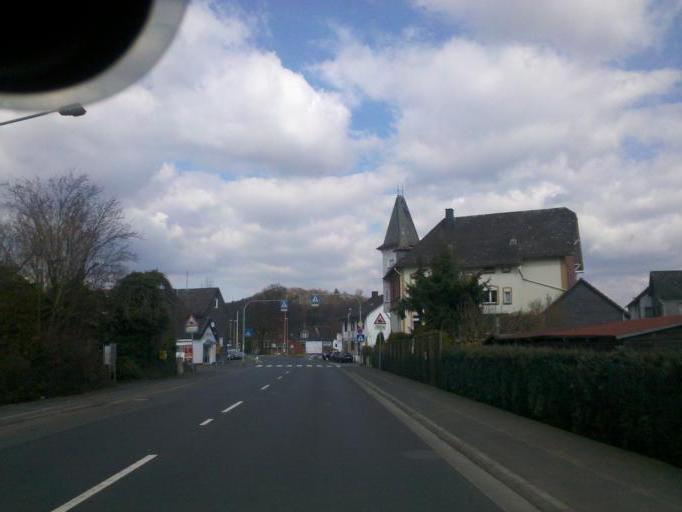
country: DE
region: Hesse
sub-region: Regierungsbezirk Giessen
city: Biedenkopf
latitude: 50.8560
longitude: 8.5606
